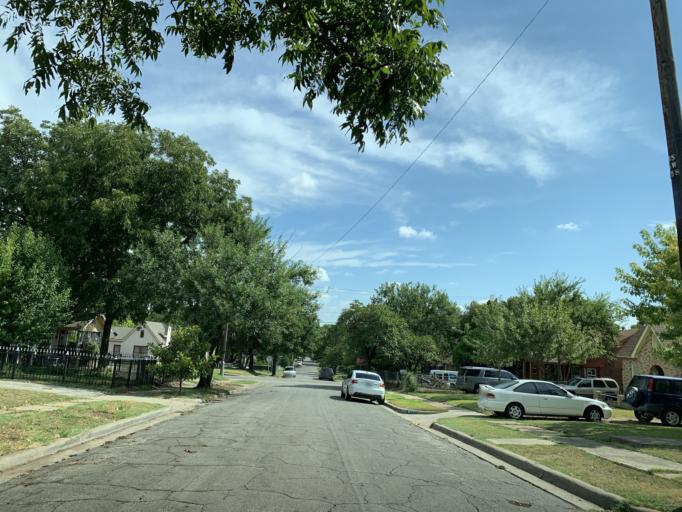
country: US
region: Texas
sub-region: Dallas County
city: Cockrell Hill
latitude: 32.7378
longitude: -96.8455
